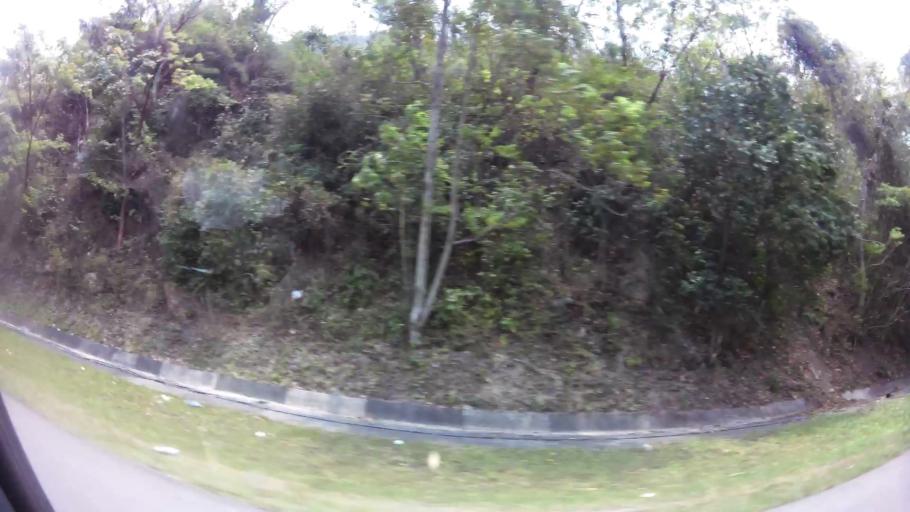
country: HN
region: Comayagua
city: Taulabe
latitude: 14.7419
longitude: -87.9629
